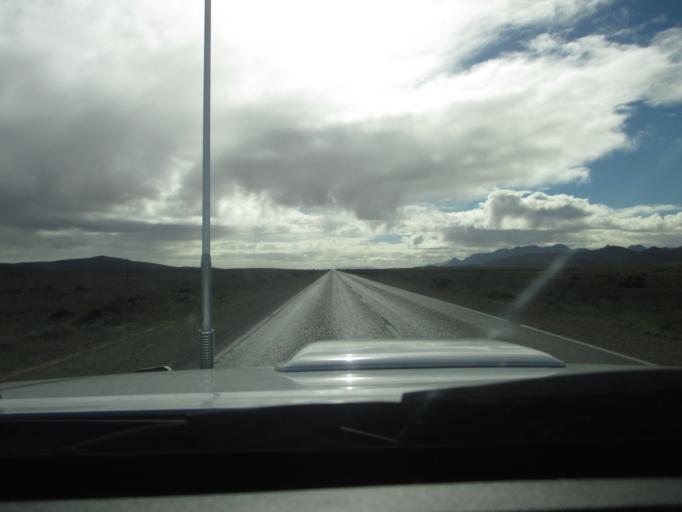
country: AU
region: South Australia
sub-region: Flinders Ranges
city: Quorn
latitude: -31.6603
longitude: 138.3753
